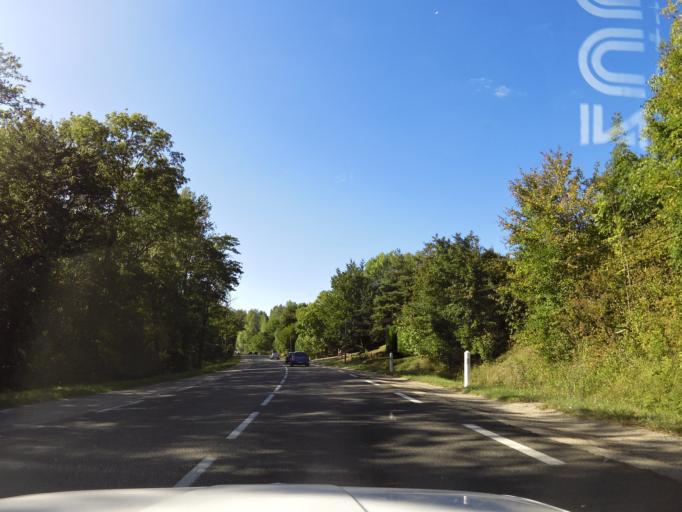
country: FR
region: Rhone-Alpes
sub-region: Departement de l'Ain
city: Vaux-en-Bugey
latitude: 45.9439
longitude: 5.3740
